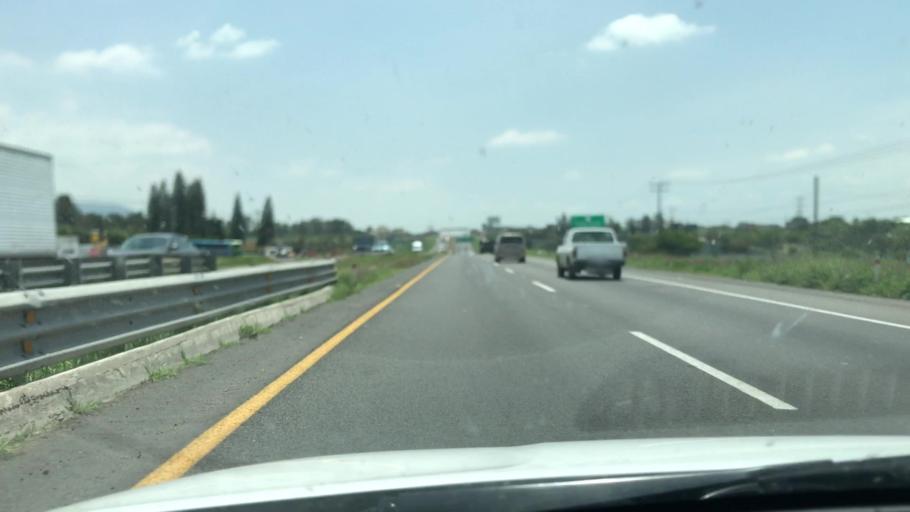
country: MX
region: Guanajuato
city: Penjamo
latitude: 20.4108
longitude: -101.7350
